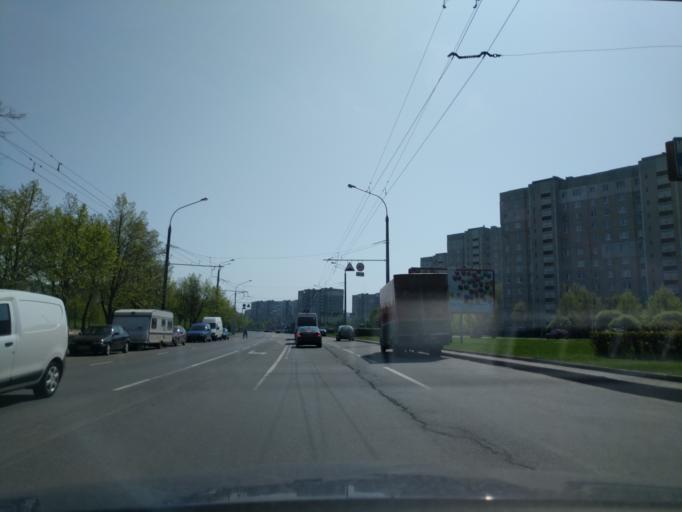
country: BY
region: Minsk
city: Malinovka
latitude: 53.8619
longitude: 27.4588
